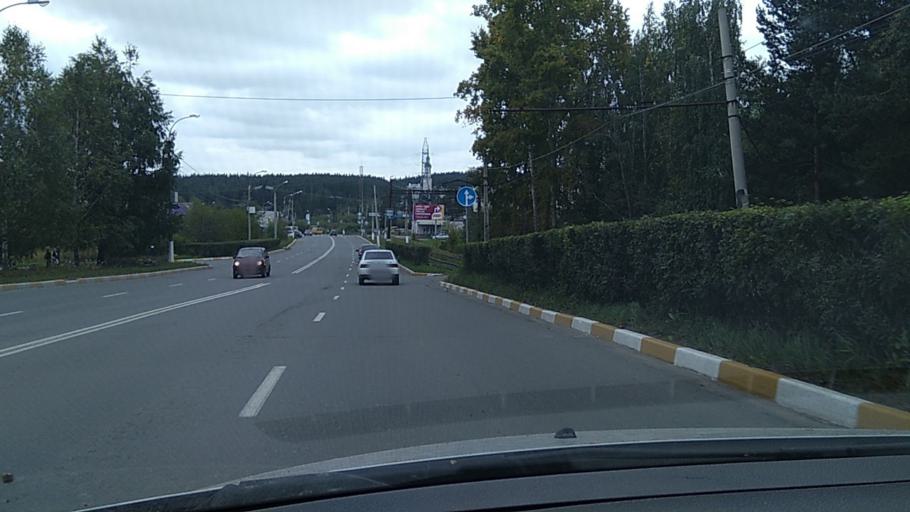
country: RU
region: Chelyabinsk
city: Zlatoust
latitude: 55.1400
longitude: 59.6683
